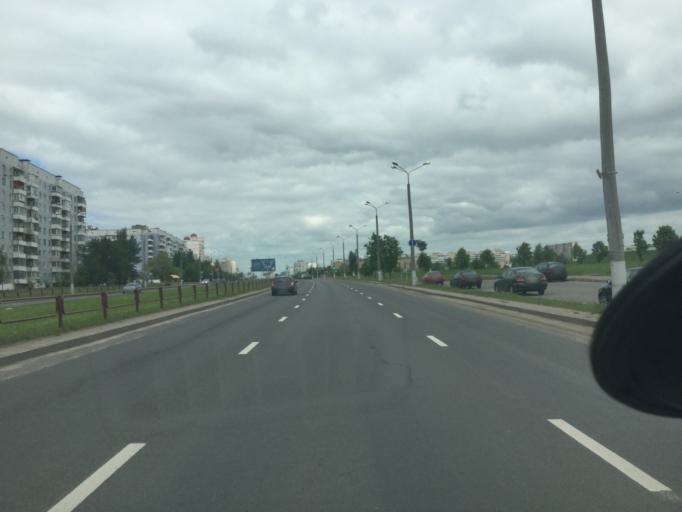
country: BY
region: Vitebsk
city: Vitebsk
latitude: 55.1630
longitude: 30.2225
